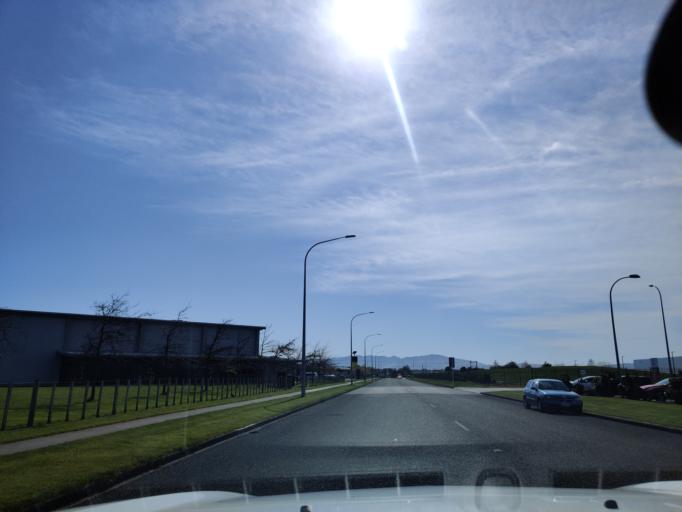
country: NZ
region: Manawatu-Wanganui
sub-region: Palmerston North City
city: Palmerston North
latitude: -40.3321
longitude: 175.6488
